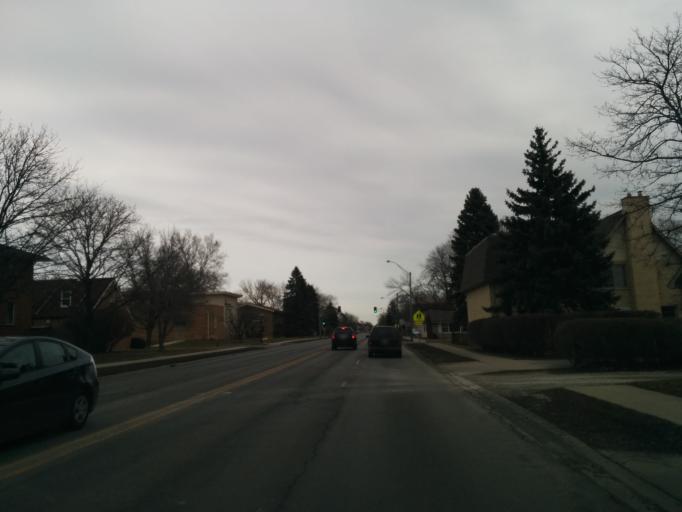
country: US
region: Illinois
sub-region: Cook County
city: La Grange Park
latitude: 41.8347
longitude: -87.8576
